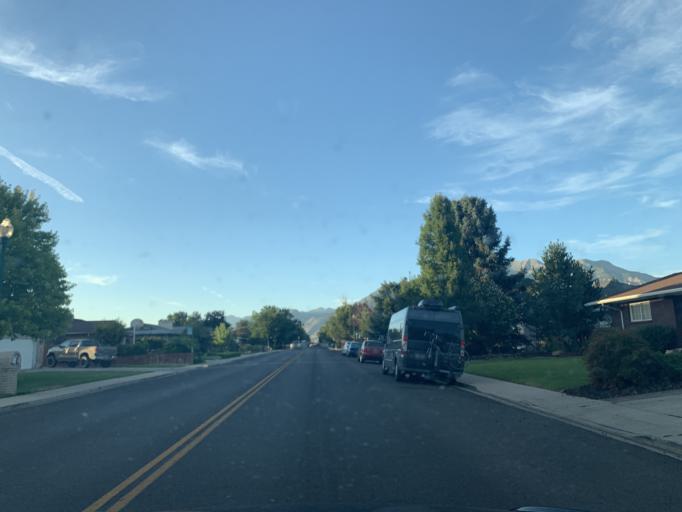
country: US
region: Utah
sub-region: Utah County
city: Orem
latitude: 40.2631
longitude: -111.6949
